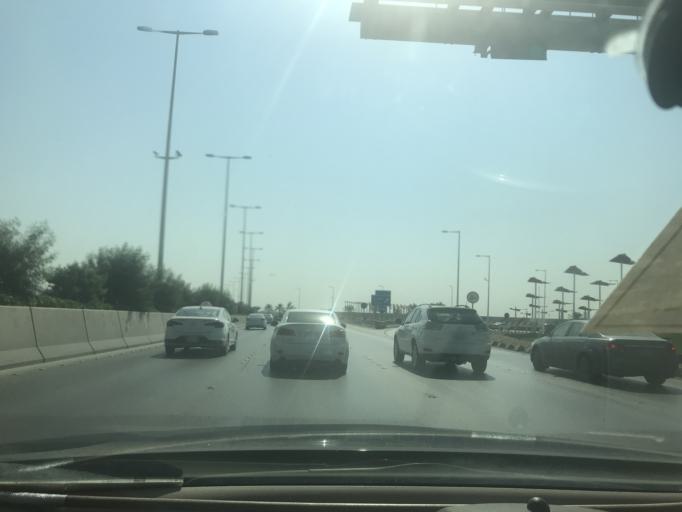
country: SA
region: Ar Riyad
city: Riyadh
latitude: 24.7263
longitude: 46.7099
